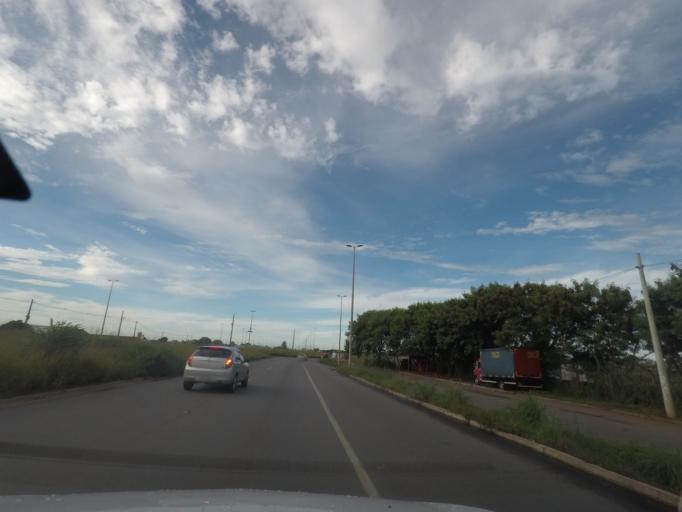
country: BR
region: Goias
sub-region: Aparecida De Goiania
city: Aparecida de Goiania
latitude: -16.7721
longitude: -49.3517
